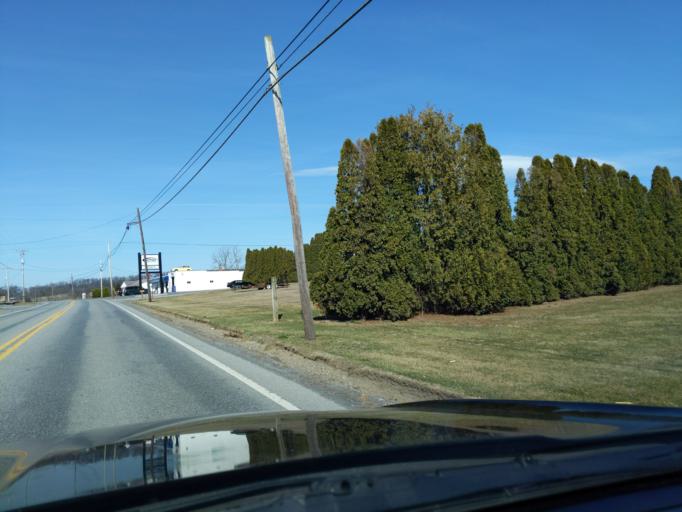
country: US
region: Pennsylvania
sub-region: Blair County
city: Martinsburg
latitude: 40.3090
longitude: -78.2890
